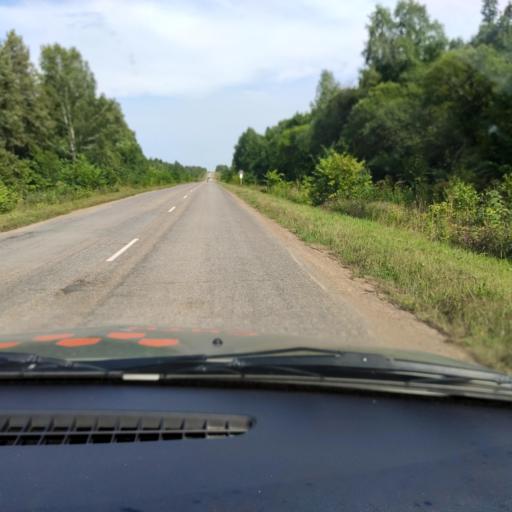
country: RU
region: Bashkortostan
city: Pavlovka
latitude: 55.3878
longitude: 56.5139
